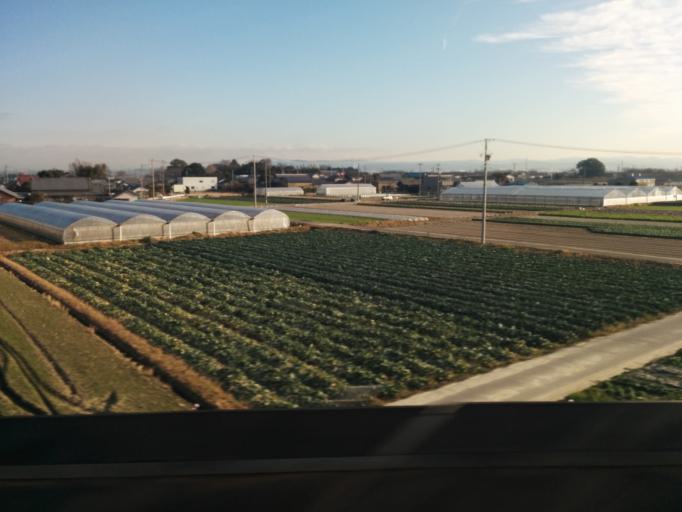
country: JP
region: Aichi
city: Anjo
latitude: 34.9221
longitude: 137.1037
